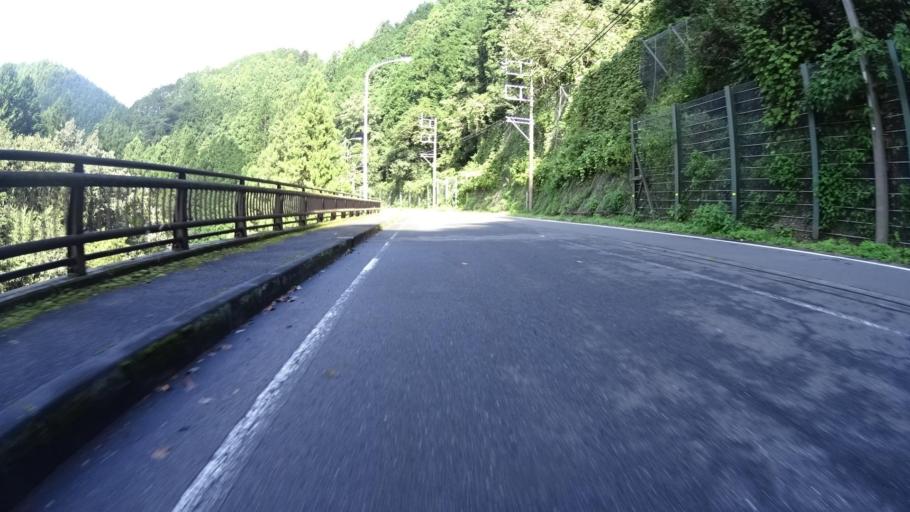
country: JP
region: Yamanashi
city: Uenohara
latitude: 35.7369
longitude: 139.0921
